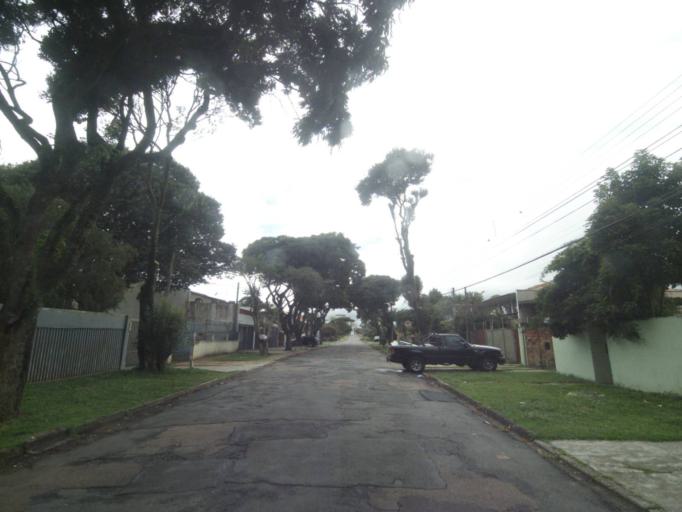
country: BR
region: Parana
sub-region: Curitiba
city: Curitiba
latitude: -25.4863
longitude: -49.3019
